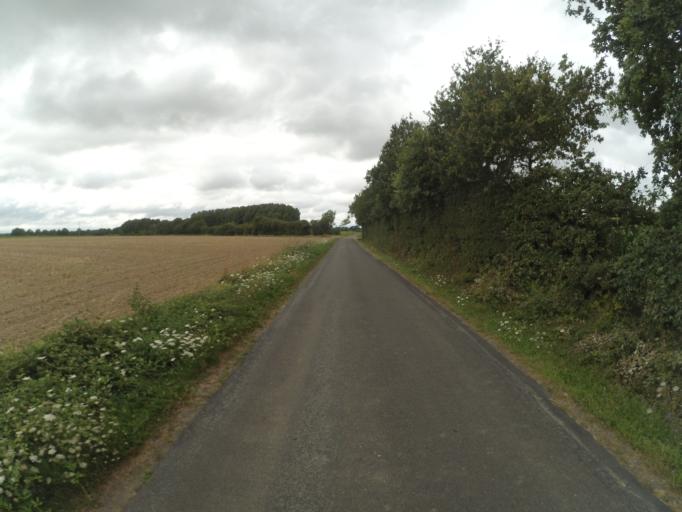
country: FR
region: Pays de la Loire
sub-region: Departement de la Vendee
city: Saint-Philbert-de-Bouaine
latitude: 46.9986
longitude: -1.5258
